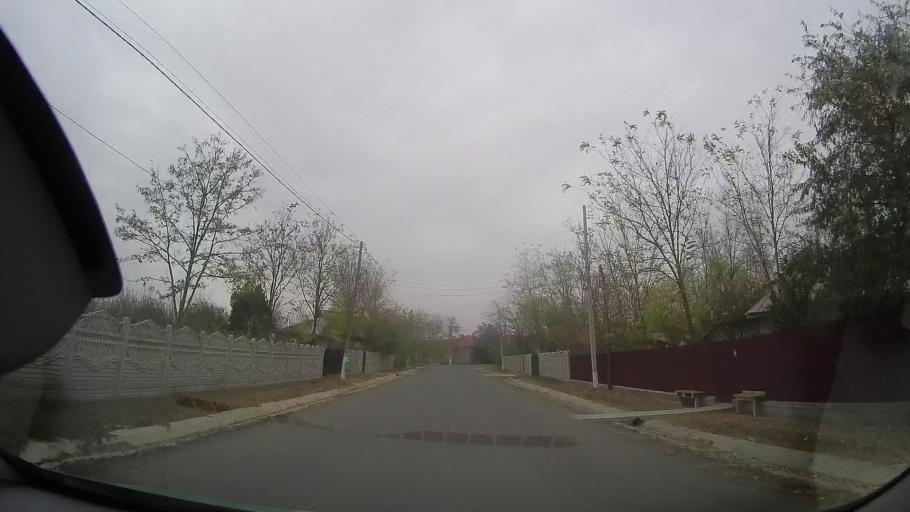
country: RO
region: Braila
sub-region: Comuna Ciocile
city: Ciocile
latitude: 44.8041
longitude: 27.2725
